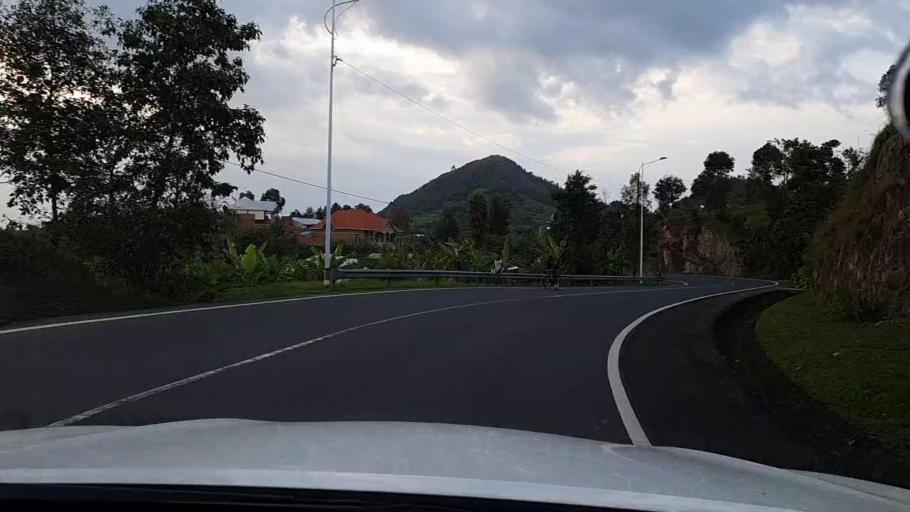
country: RW
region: Western Province
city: Kibuye
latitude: -2.0867
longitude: 29.4102
